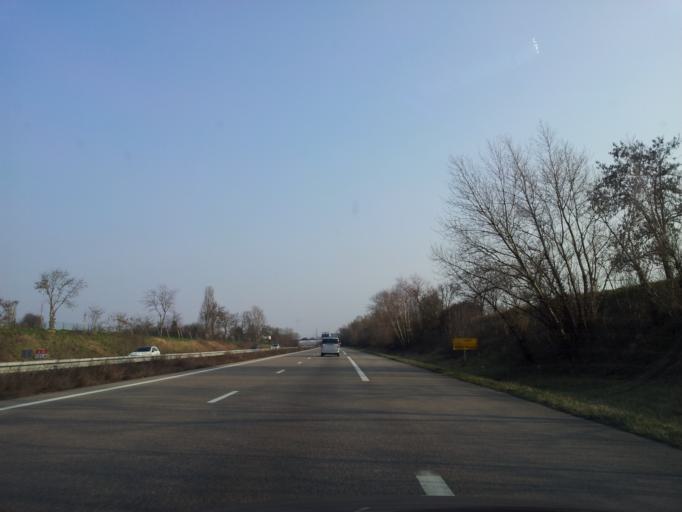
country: FR
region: Alsace
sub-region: Departement du Haut-Rhin
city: Blotzheim
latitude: 47.6101
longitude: 7.5232
